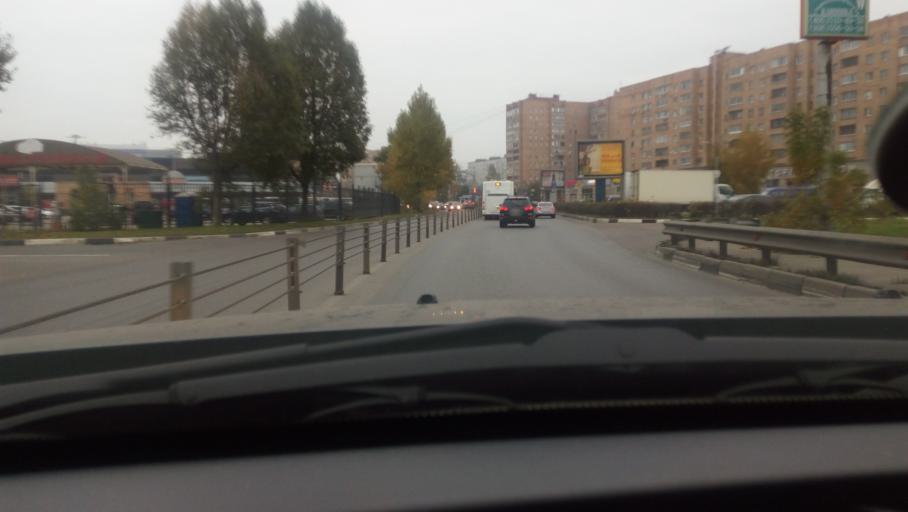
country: RU
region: Moskovskaya
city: Zheleznodorozhnyy
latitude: 55.7513
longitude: 38.0051
